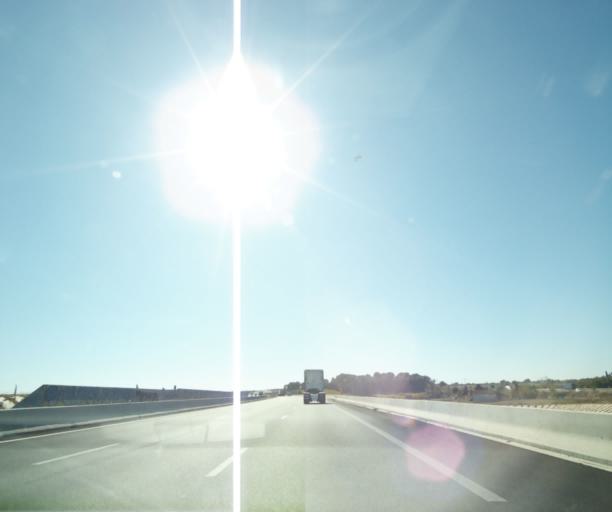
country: FR
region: Languedoc-Roussillon
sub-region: Departement de l'Herault
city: Saint-Aunes
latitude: 43.6183
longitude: 3.9526
